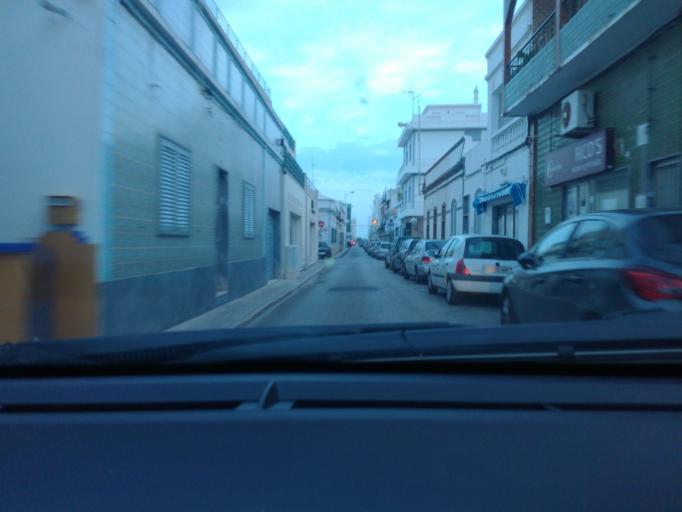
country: PT
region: Faro
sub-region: Olhao
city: Laranjeiro
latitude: 37.0567
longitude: -7.7479
